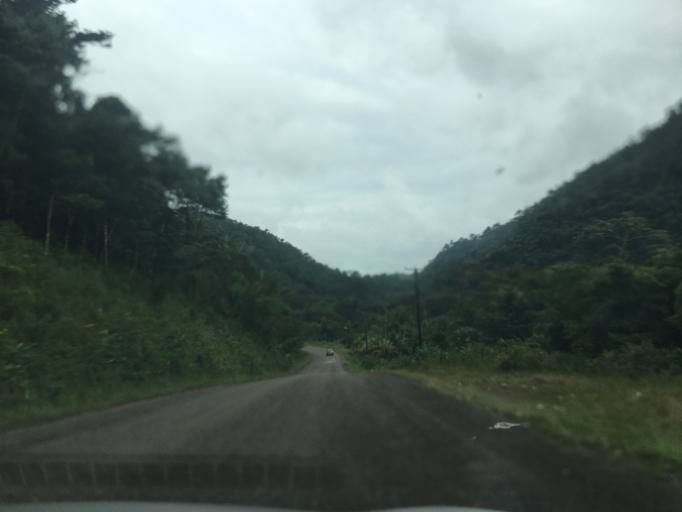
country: BZ
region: Cayo
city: Belmopan
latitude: 17.0569
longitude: -88.5861
